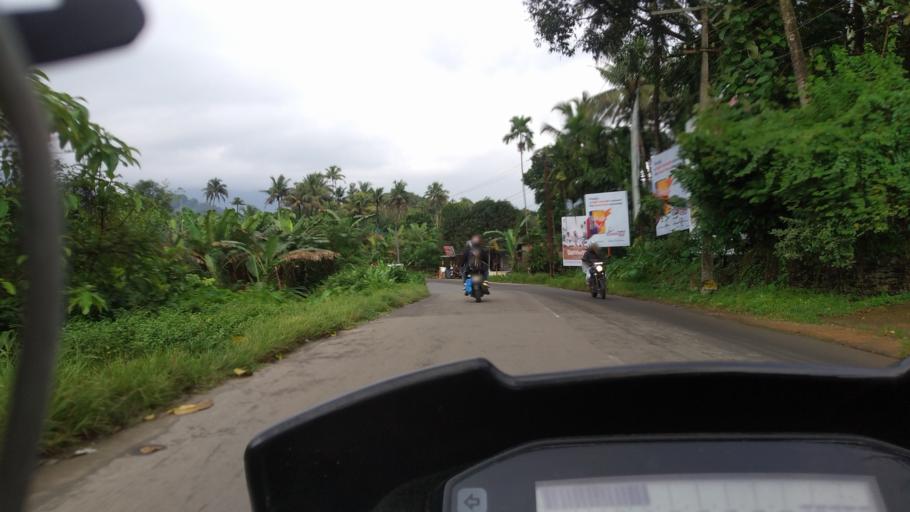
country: IN
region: Kerala
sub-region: Idukki
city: Kuttampuzha
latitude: 10.0506
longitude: 76.7366
